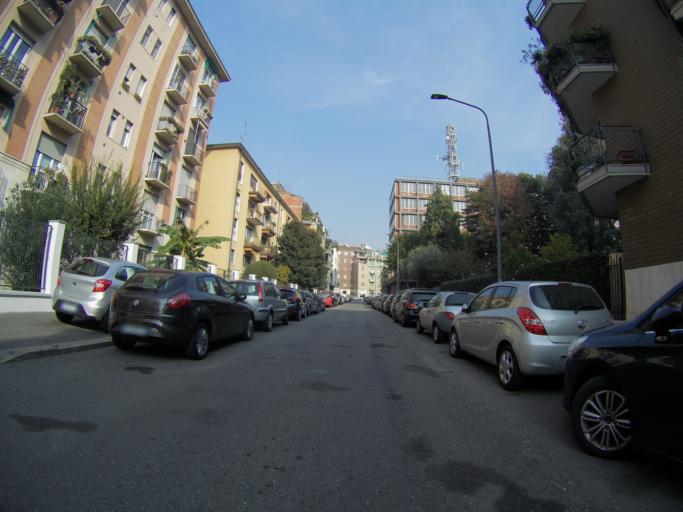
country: IT
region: Lombardy
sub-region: Citta metropolitana di Milano
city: Novegro-Tregarezzo-San Felice
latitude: 45.4818
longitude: 9.2354
